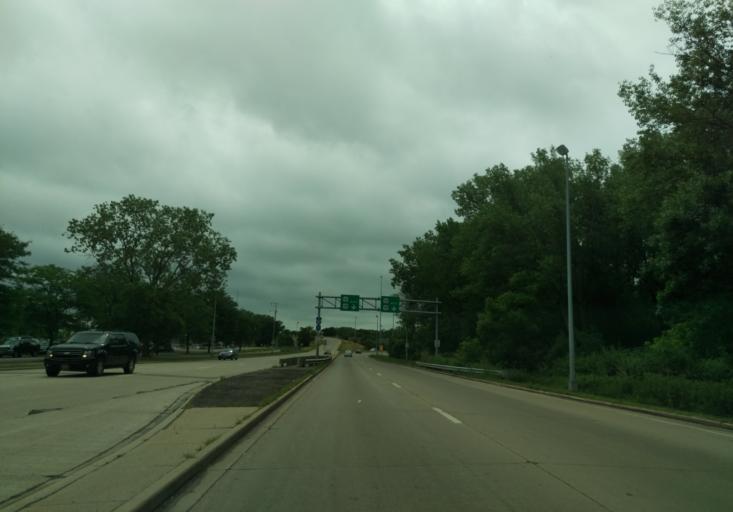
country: US
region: Wisconsin
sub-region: Dane County
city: Madison
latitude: 43.0460
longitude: -89.3731
